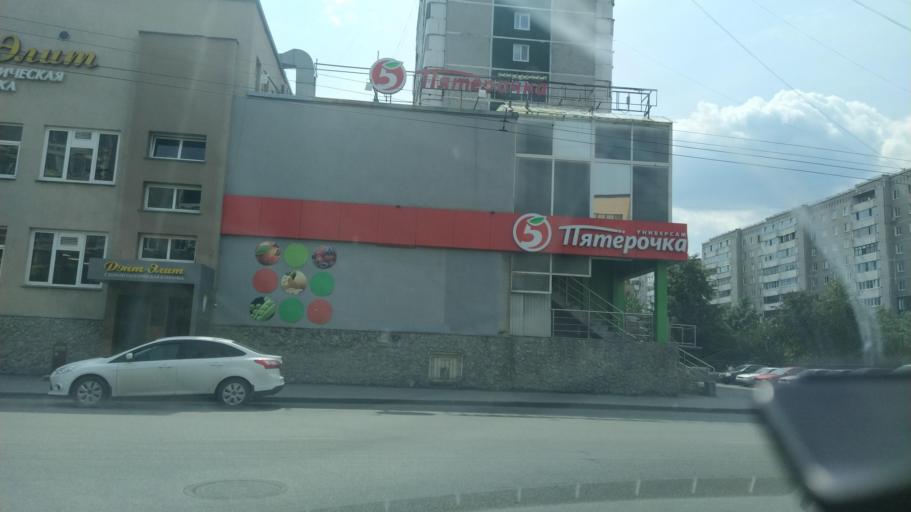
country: RU
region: Sverdlovsk
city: Yekaterinburg
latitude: 56.7925
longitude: 60.6308
